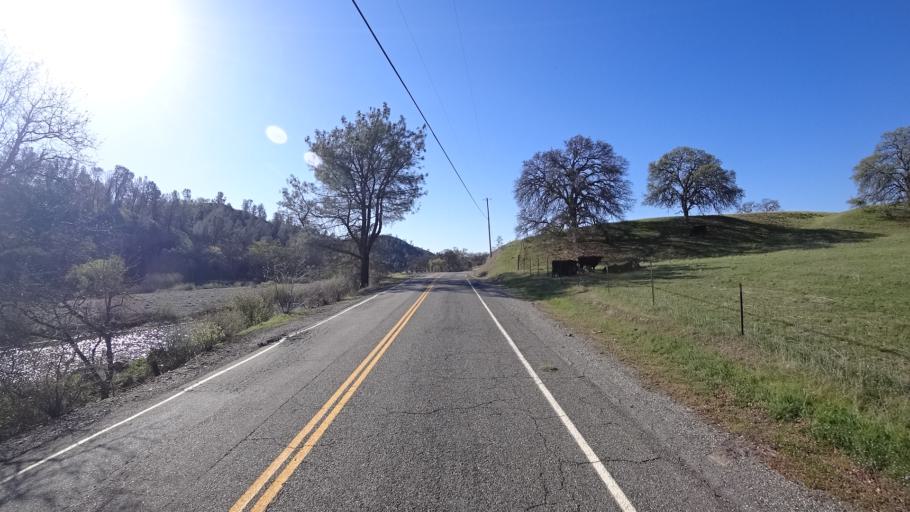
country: US
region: California
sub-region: Glenn County
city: Orland
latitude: 39.6693
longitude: -122.5255
